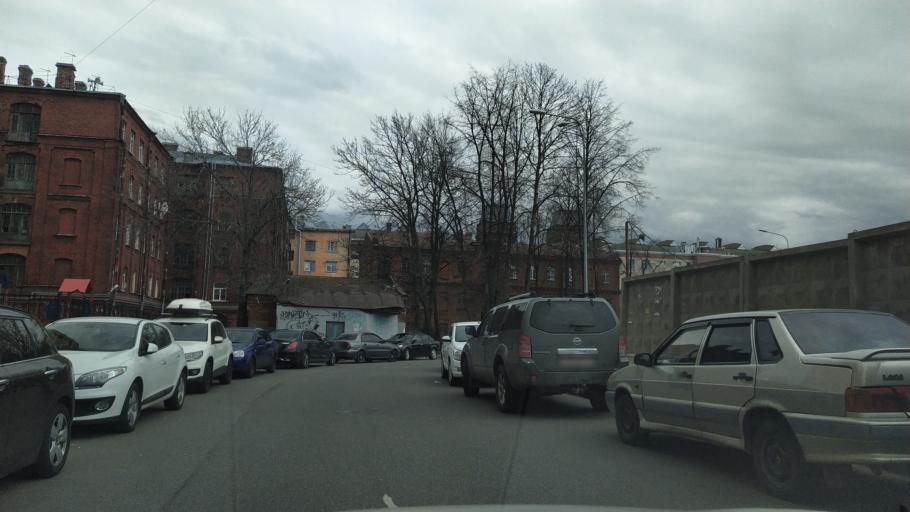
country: RU
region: St.-Petersburg
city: Centralniy
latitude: 59.9395
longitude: 30.3913
